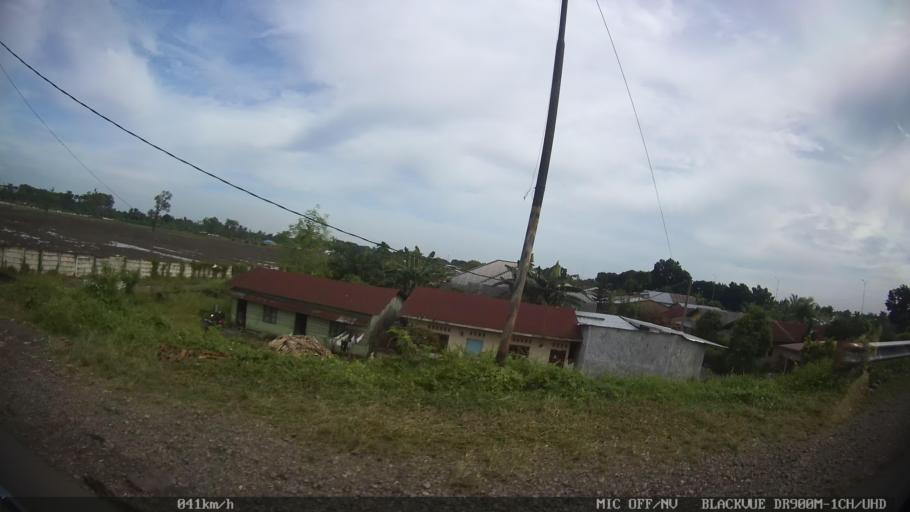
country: ID
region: North Sumatra
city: Medan
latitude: 3.6214
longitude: 98.7188
